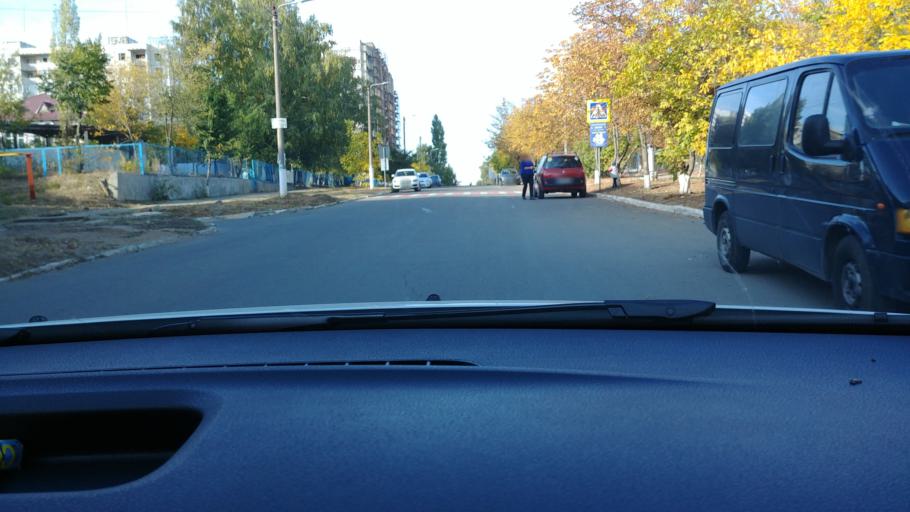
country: MD
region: Rezina
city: Rezina
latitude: 47.7465
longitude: 28.9561
